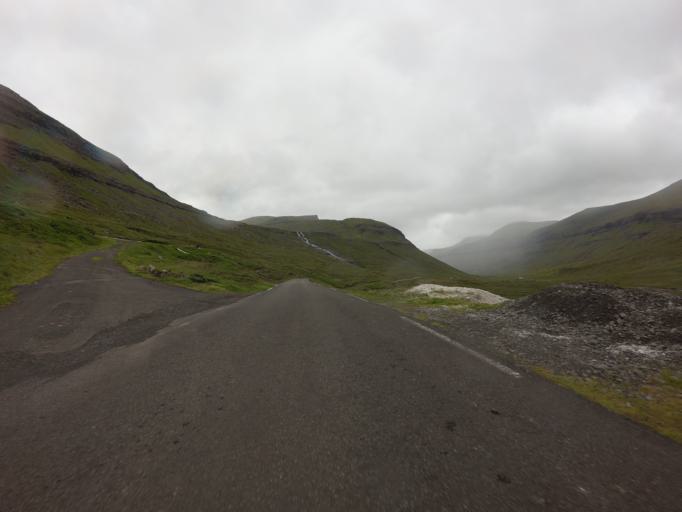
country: FO
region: Streymoy
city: Vestmanna
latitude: 62.2187
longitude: -7.1238
